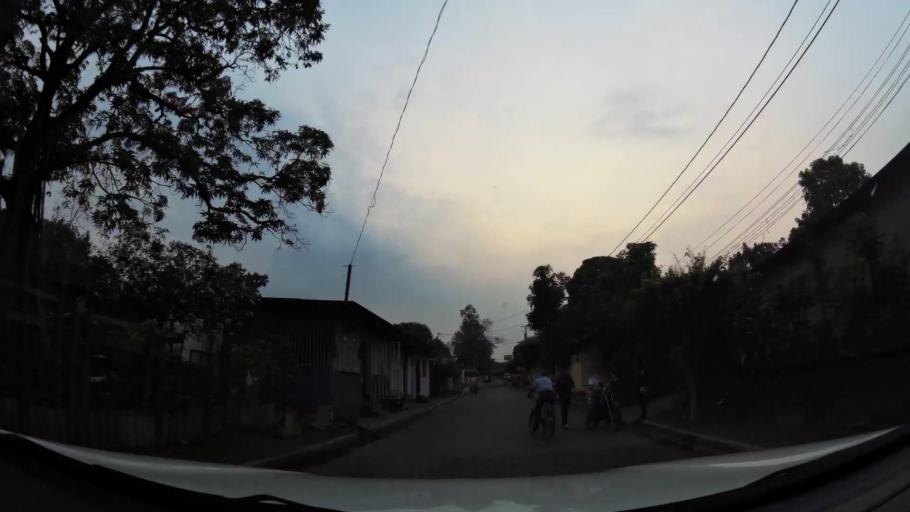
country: NI
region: Masaya
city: Nindiri
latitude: 12.0035
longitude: -86.1184
